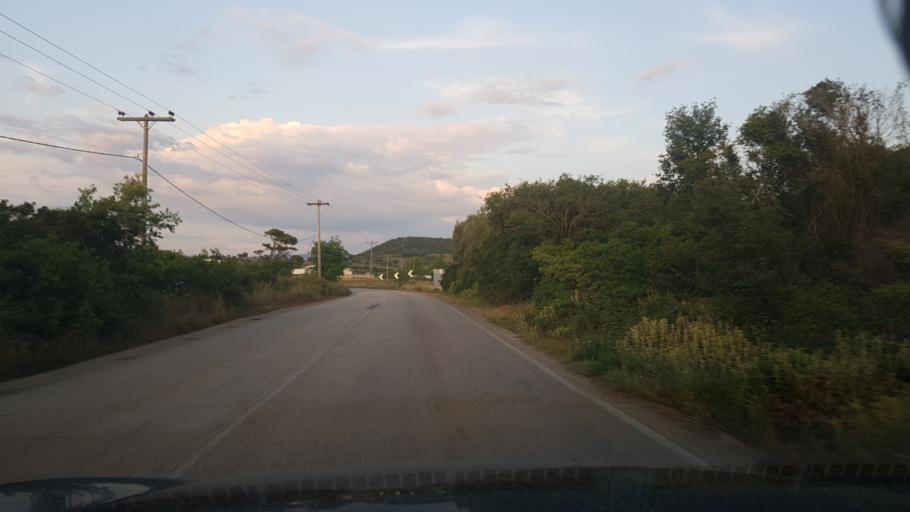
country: GR
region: Ionian Islands
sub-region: Lefkada
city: Lefkada
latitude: 38.8633
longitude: 20.7867
